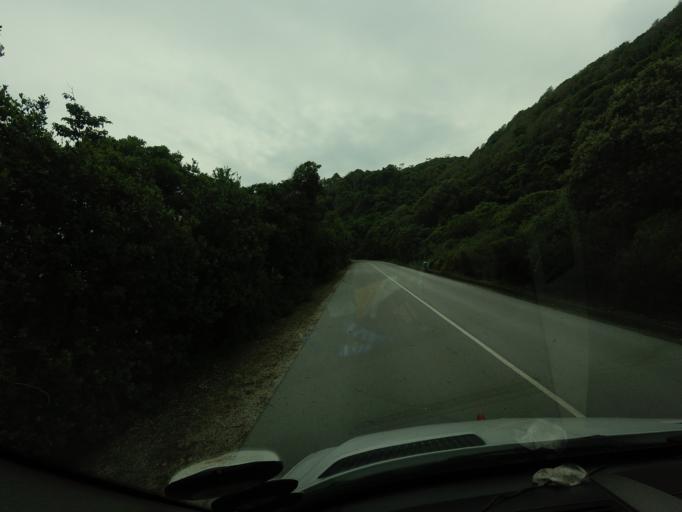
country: ZA
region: Eastern Cape
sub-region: Cacadu District Municipality
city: Kareedouw
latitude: -34.0213
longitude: 23.8838
